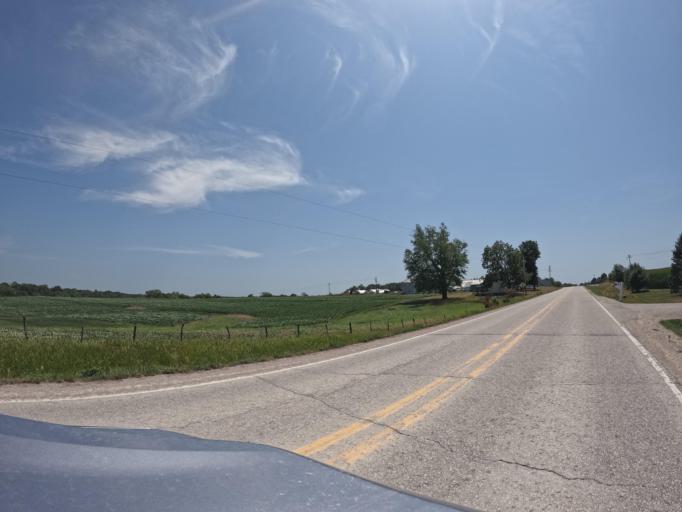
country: US
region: Iowa
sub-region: Henry County
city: Mount Pleasant
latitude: 40.9284
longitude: -91.6222
